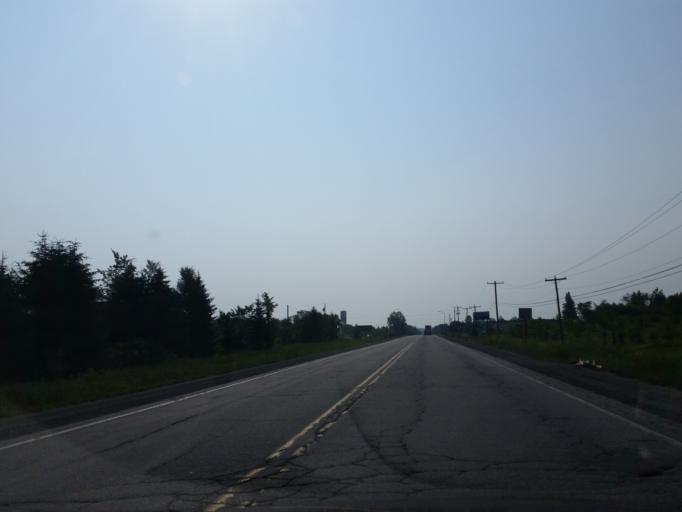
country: CA
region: Ontario
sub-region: Nipissing District
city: North Bay
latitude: 46.4154
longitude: -80.1378
